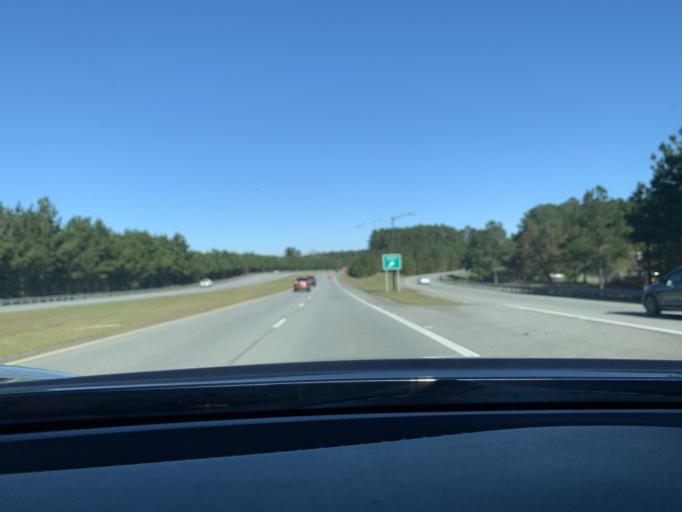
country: US
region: Georgia
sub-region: Chatham County
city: Pooler
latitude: 32.1138
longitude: -81.2679
